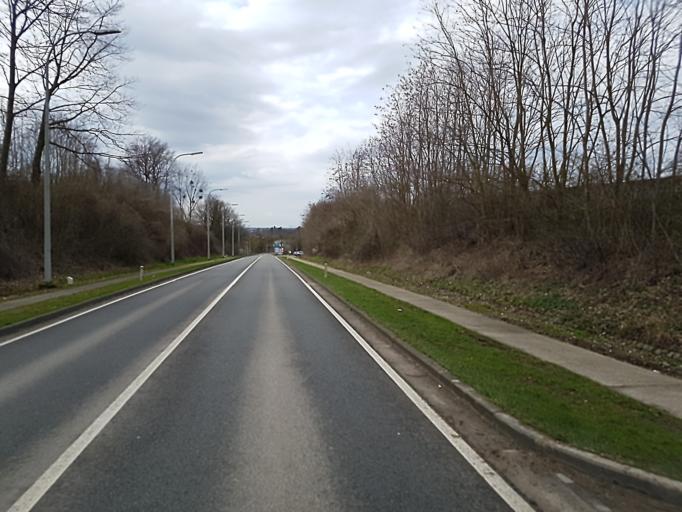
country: BE
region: Flanders
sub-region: Provincie Limburg
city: Borgloon
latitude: 50.7986
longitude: 5.3486
